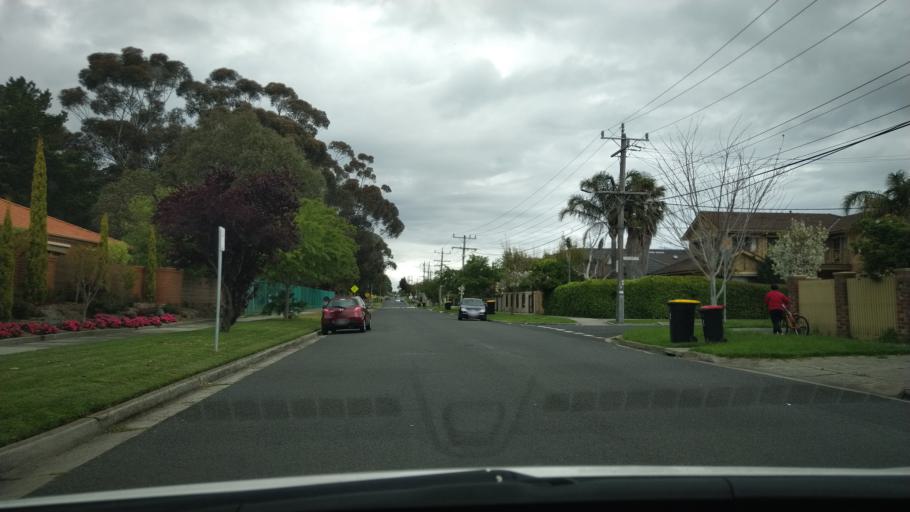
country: AU
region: Victoria
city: Highett
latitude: -37.9604
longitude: 145.0660
